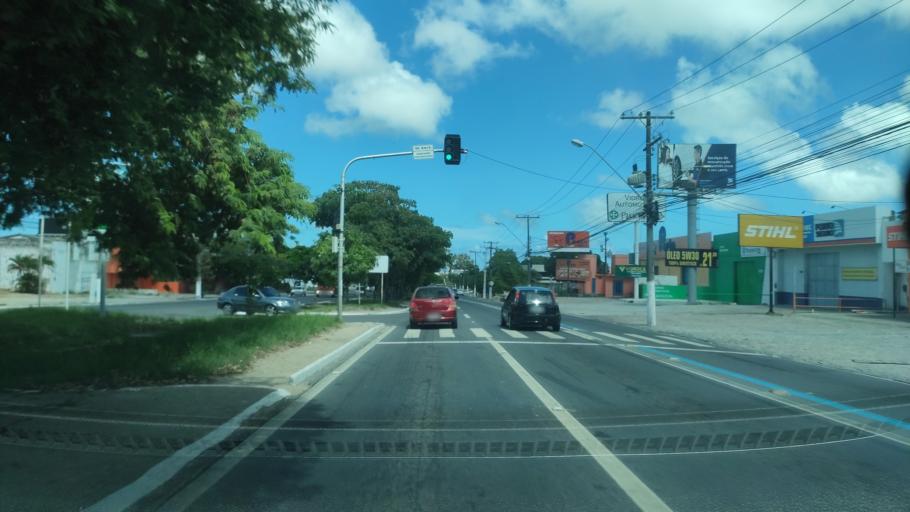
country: BR
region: Alagoas
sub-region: Maceio
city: Maceio
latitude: -9.6001
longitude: -35.7491
